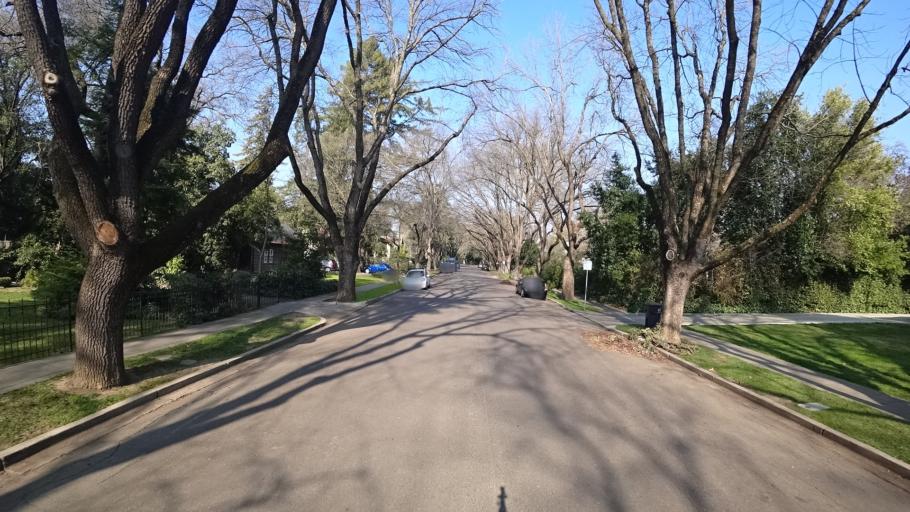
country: US
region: California
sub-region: Yolo County
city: Davis
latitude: 38.5482
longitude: -121.7514
